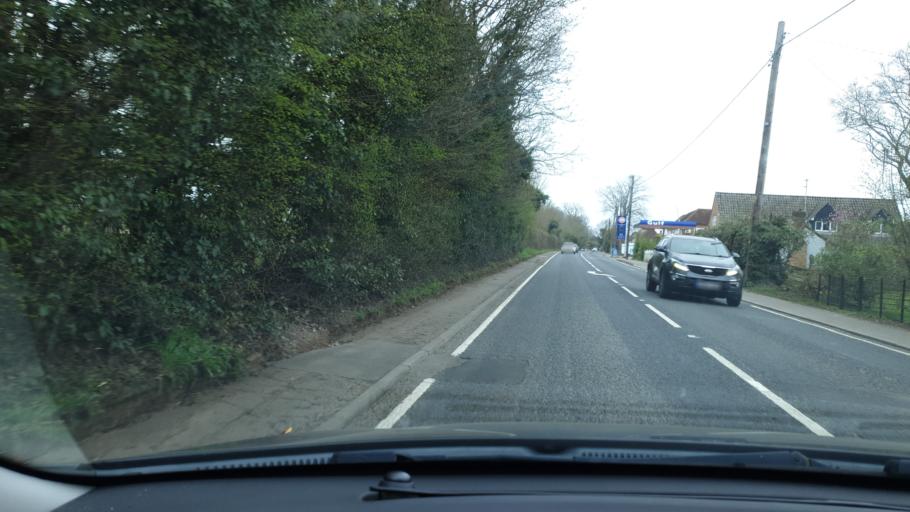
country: GB
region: England
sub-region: Essex
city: Great Horkesley
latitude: 51.9324
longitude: 0.8763
